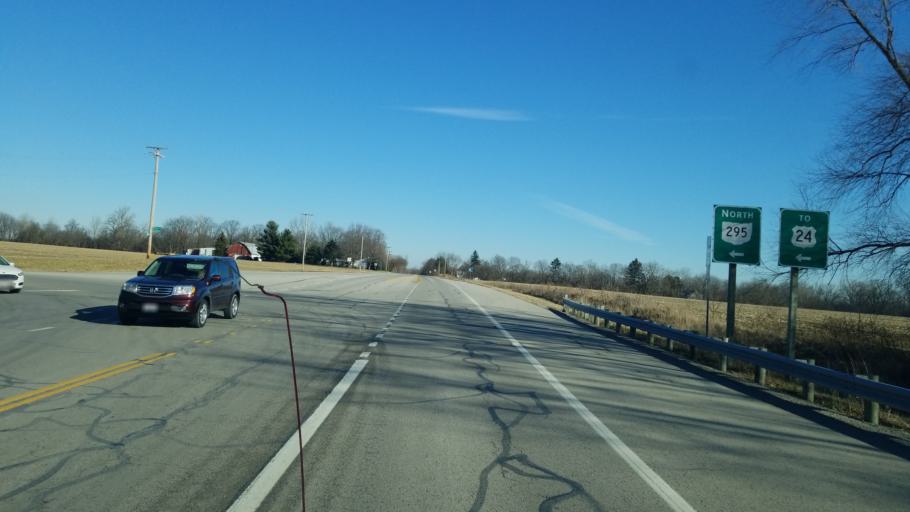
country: US
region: Ohio
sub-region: Lucas County
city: Whitehouse
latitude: 41.4350
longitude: -83.8255
